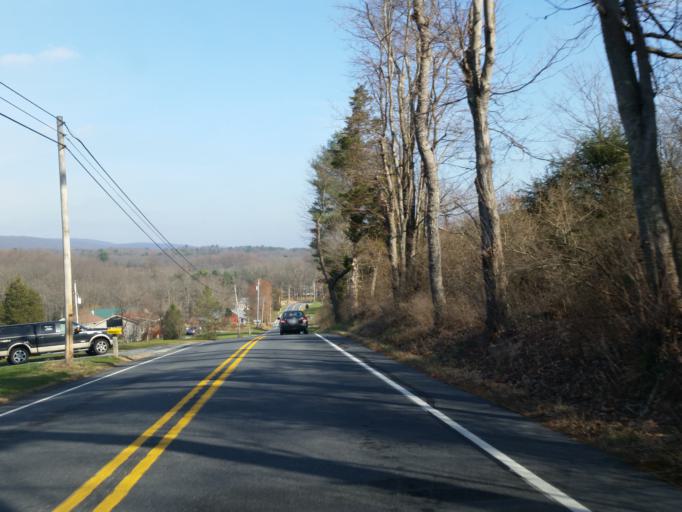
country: US
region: Pennsylvania
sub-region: Lebanon County
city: Jonestown
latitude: 40.4712
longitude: -76.5764
